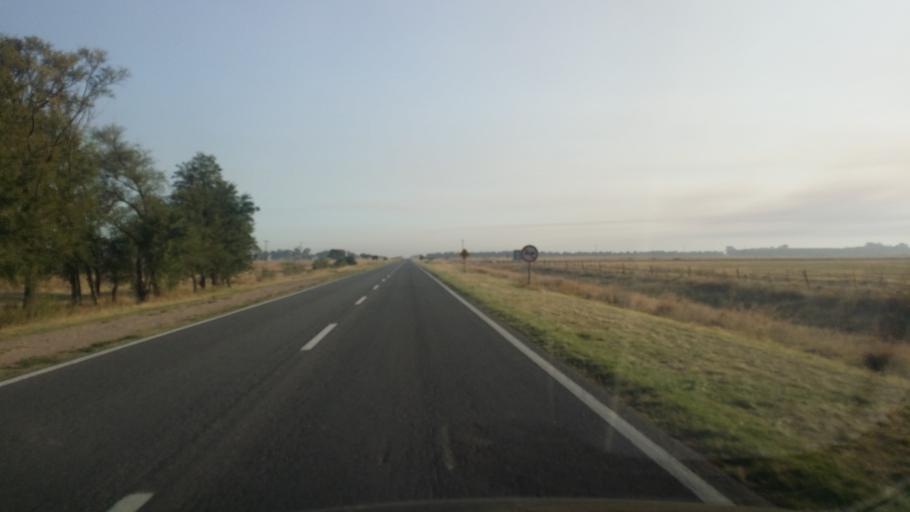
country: AR
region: La Pampa
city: Santa Rosa
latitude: -36.4837
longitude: -64.2805
